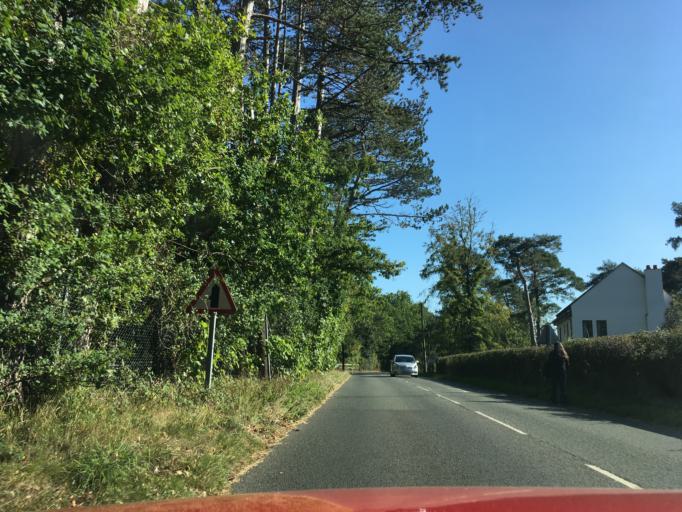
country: GB
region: England
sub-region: West Berkshire
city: Hermitage
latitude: 51.4396
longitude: -1.2743
